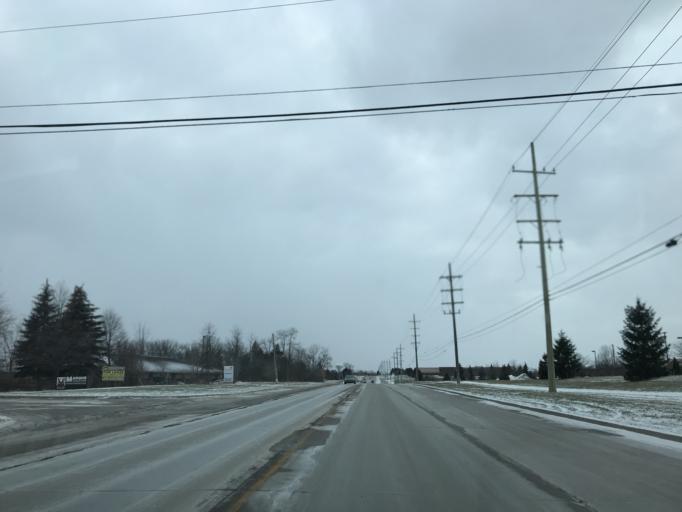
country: US
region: Michigan
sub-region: Wayne County
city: Plymouth
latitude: 42.3951
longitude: -83.4969
